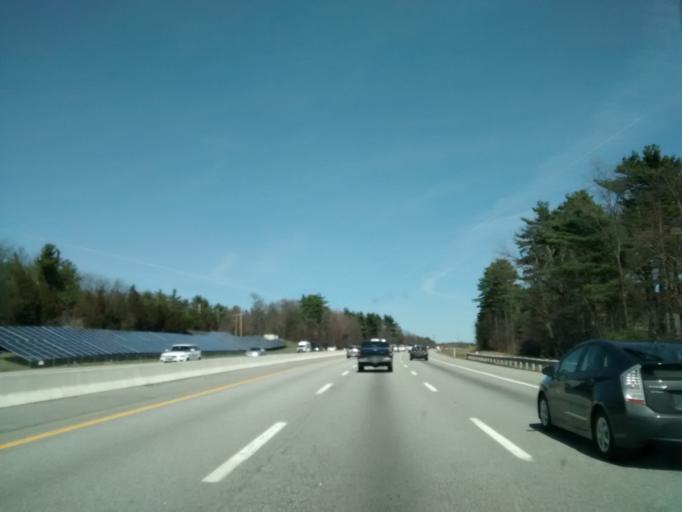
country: US
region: Massachusetts
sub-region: Middlesex County
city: Cochituate
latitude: 42.3257
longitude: -71.3347
